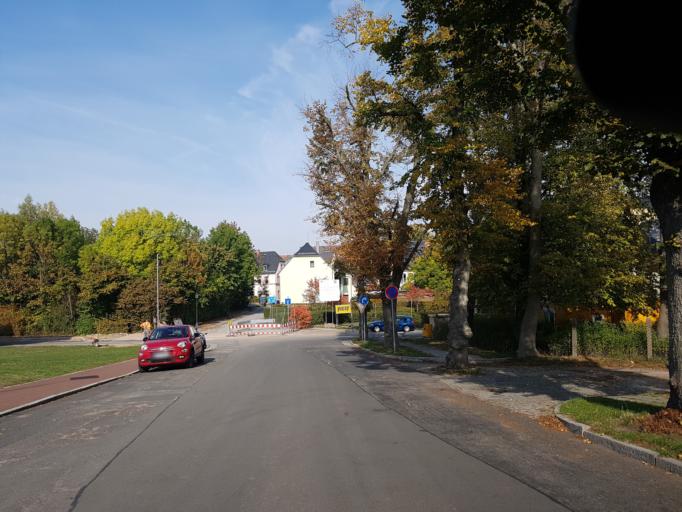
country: DE
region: Saxony
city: Hartha
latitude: 51.0964
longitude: 12.9774
